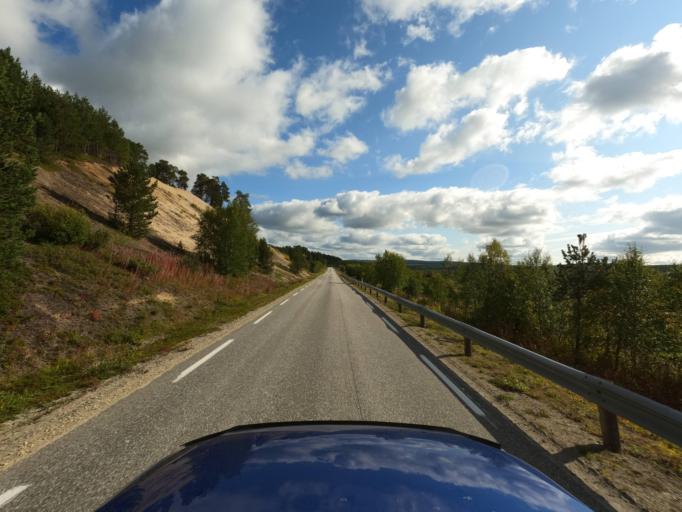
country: NO
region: Finnmark Fylke
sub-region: Karasjok
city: Karasjohka
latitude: 69.4438
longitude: 25.2202
